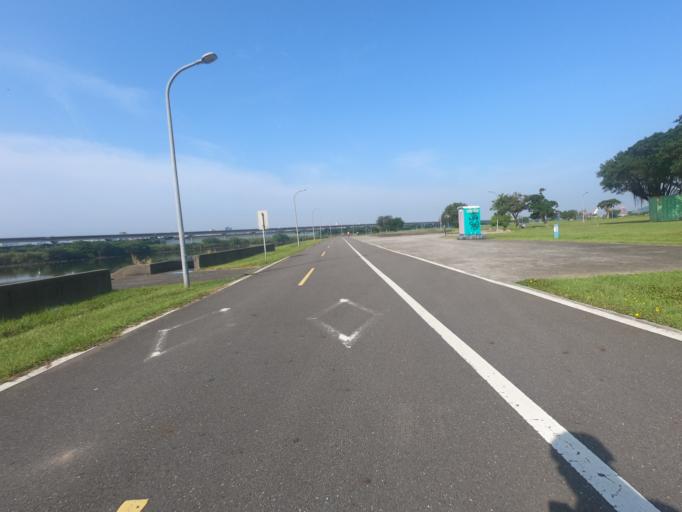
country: TW
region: Taipei
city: Taipei
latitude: 25.0743
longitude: 121.5643
